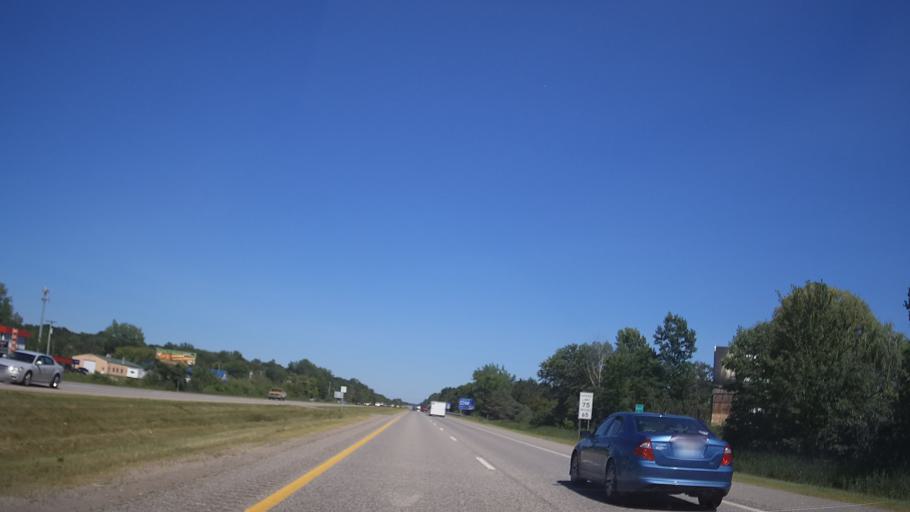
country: US
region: Michigan
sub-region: Midland County
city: Midland
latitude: 43.6561
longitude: -84.2958
